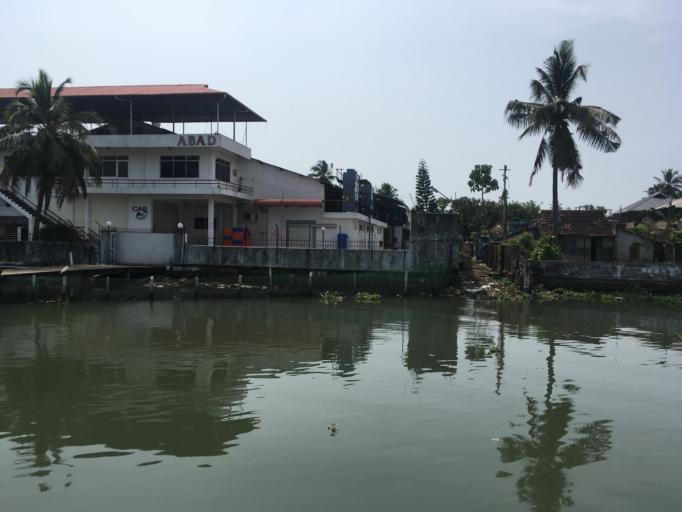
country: IN
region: Kerala
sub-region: Ernakulam
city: Cochin
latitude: 9.9778
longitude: 76.2423
